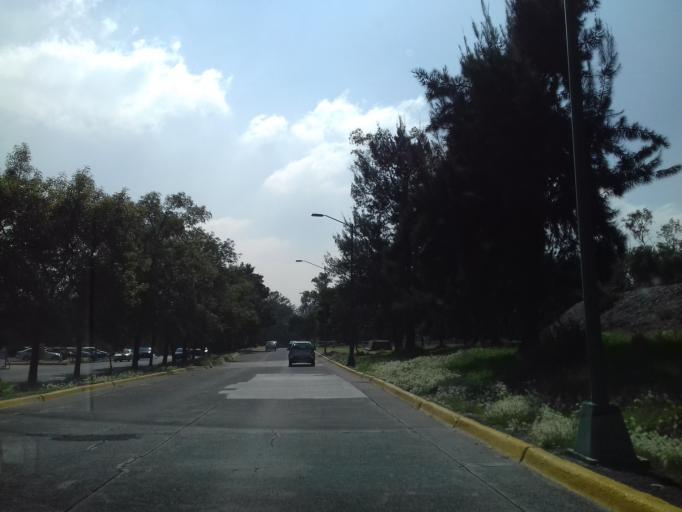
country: MX
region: Mexico City
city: Magdalena Contreras
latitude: 19.3297
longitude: -99.1942
